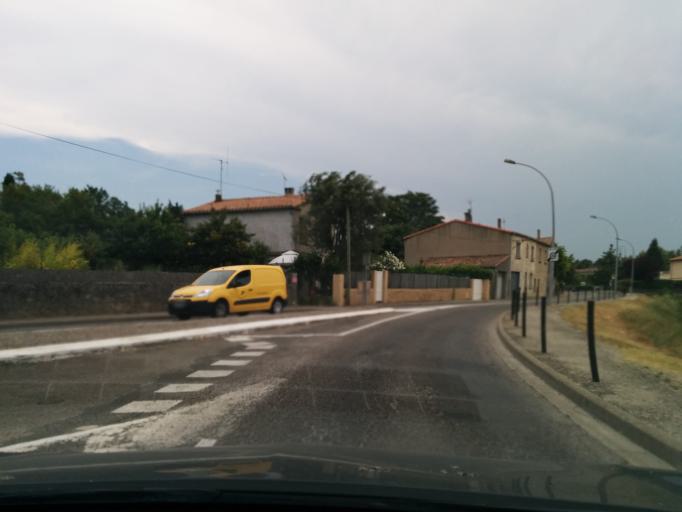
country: FR
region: Languedoc-Roussillon
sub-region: Departement de l'Aude
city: Carcassonne
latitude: 43.2038
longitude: 2.3601
